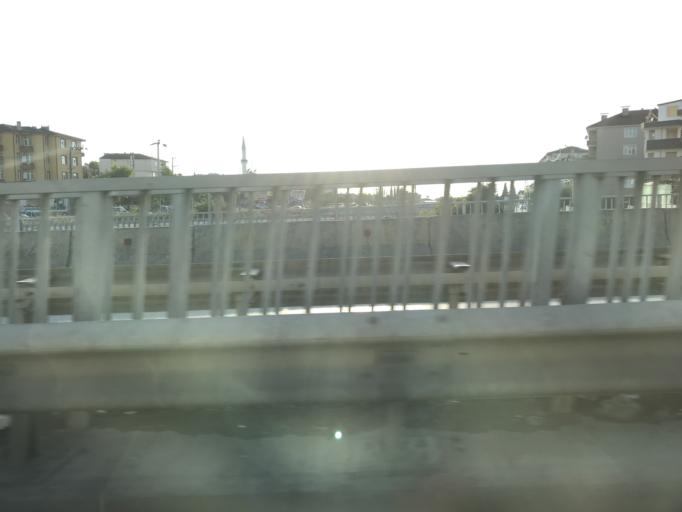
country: TR
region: Kocaeli
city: Darica
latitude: 40.7824
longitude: 29.4166
